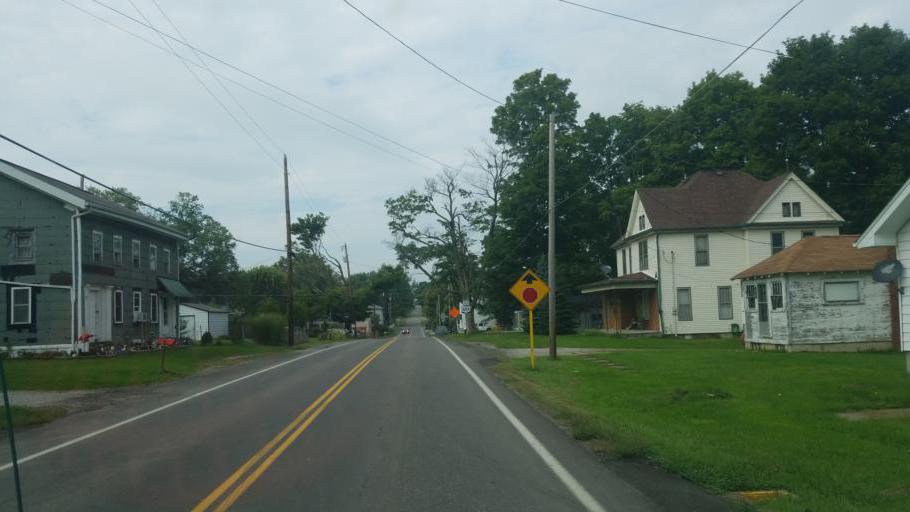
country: US
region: Ohio
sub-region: Wayne County
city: West Salem
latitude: 40.9237
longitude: -82.0521
